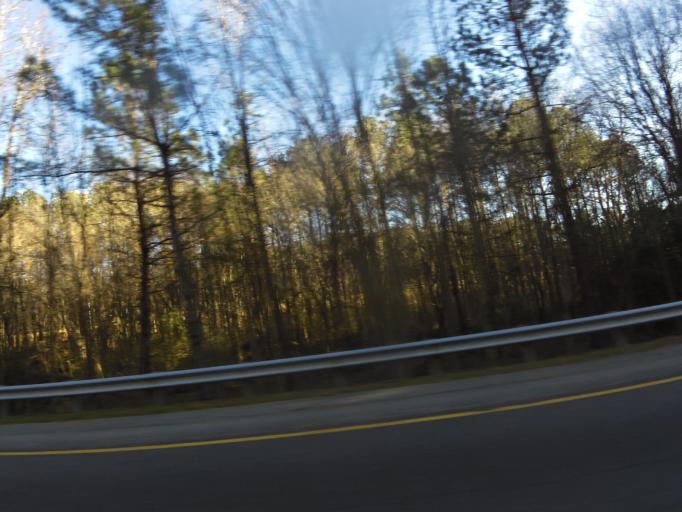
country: US
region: Virginia
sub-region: City of Portsmouth
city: Portsmouth Heights
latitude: 36.7887
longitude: -76.3990
